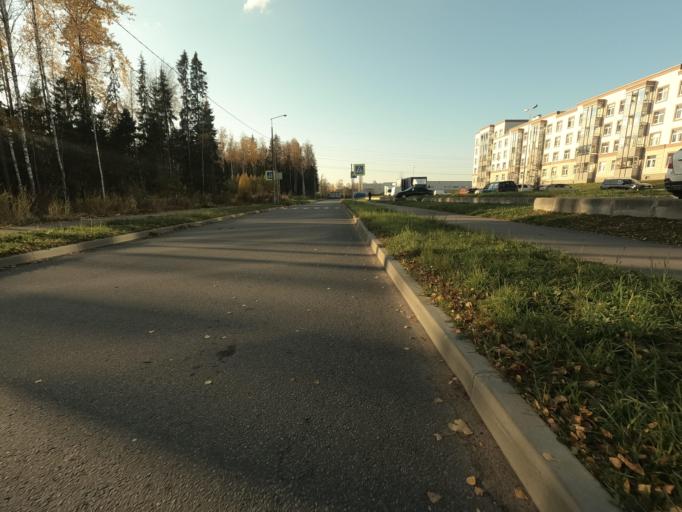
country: RU
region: Leningrad
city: Sertolovo
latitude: 60.1640
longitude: 30.1888
